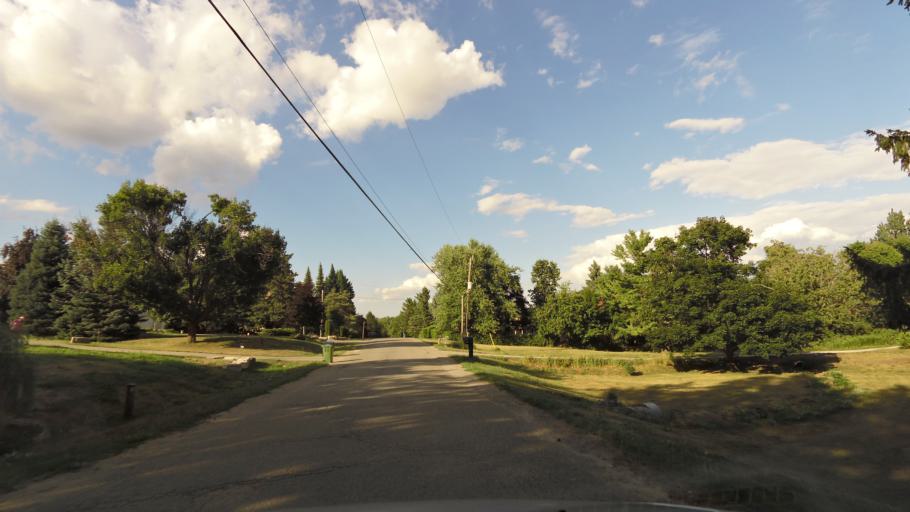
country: CA
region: Ontario
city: Brampton
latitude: 43.7618
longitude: -79.9276
